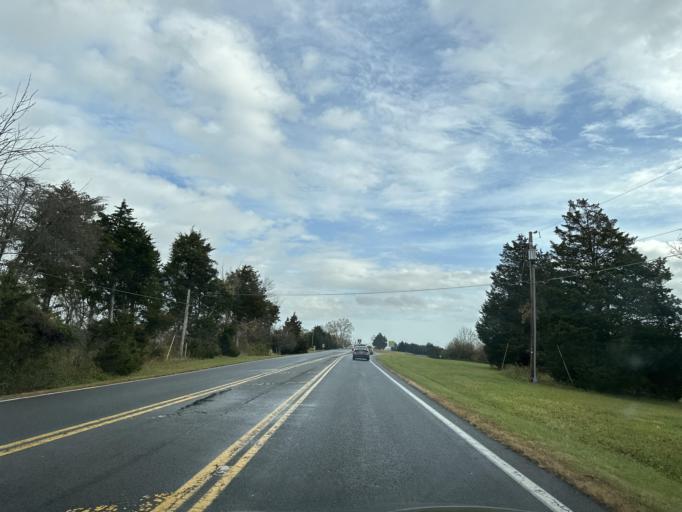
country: US
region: Virginia
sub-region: Shenandoah County
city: Strasburg
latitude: 38.9730
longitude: -78.4022
